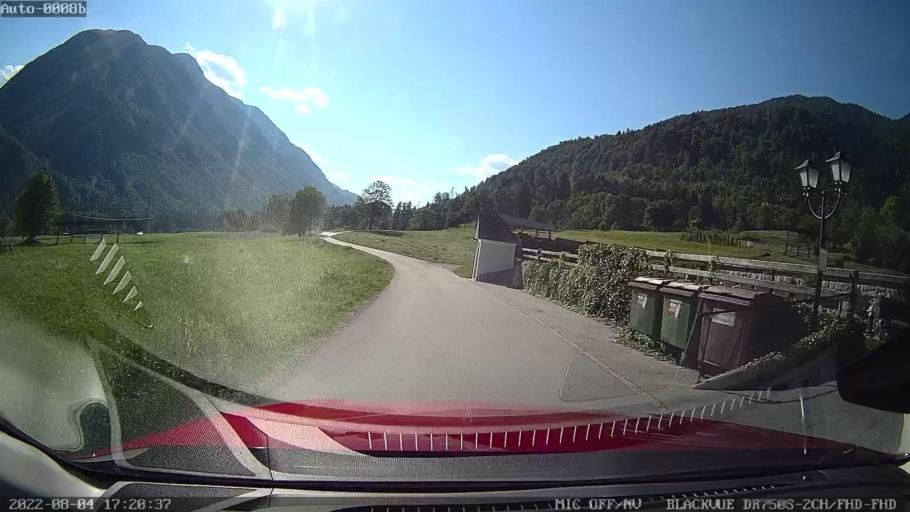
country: SI
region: Kranjska Gora
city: Mojstrana
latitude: 46.4675
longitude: 13.9411
